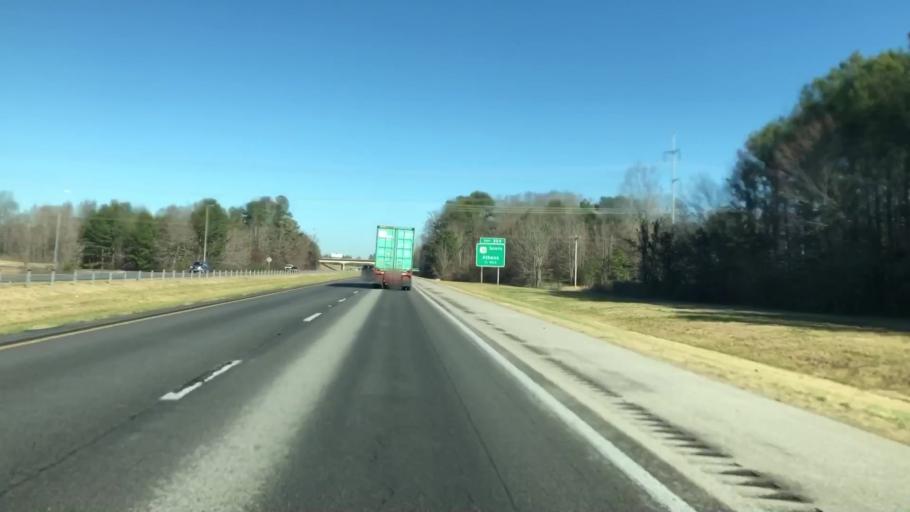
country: US
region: Alabama
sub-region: Limestone County
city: Athens
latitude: 34.8228
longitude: -86.9387
